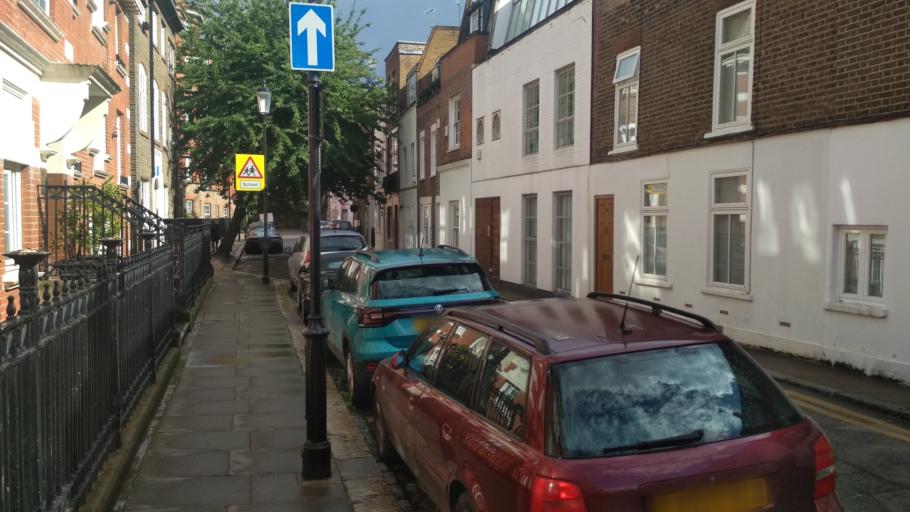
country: GB
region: England
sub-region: Greater London
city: Chelsea
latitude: 51.4914
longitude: -0.1709
